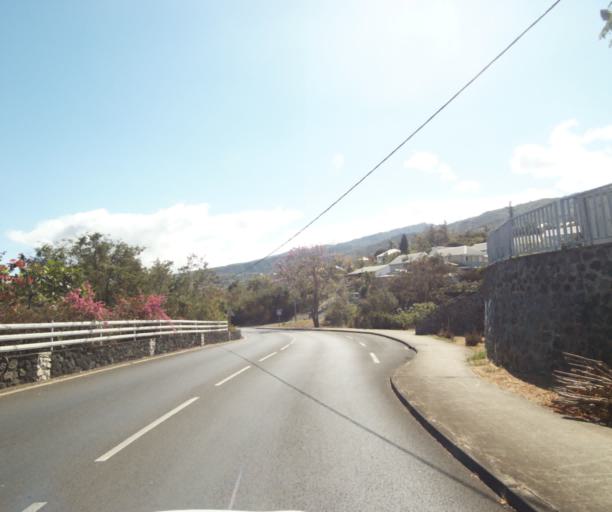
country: RE
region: Reunion
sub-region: Reunion
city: La Possession
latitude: -20.9891
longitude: 55.3307
